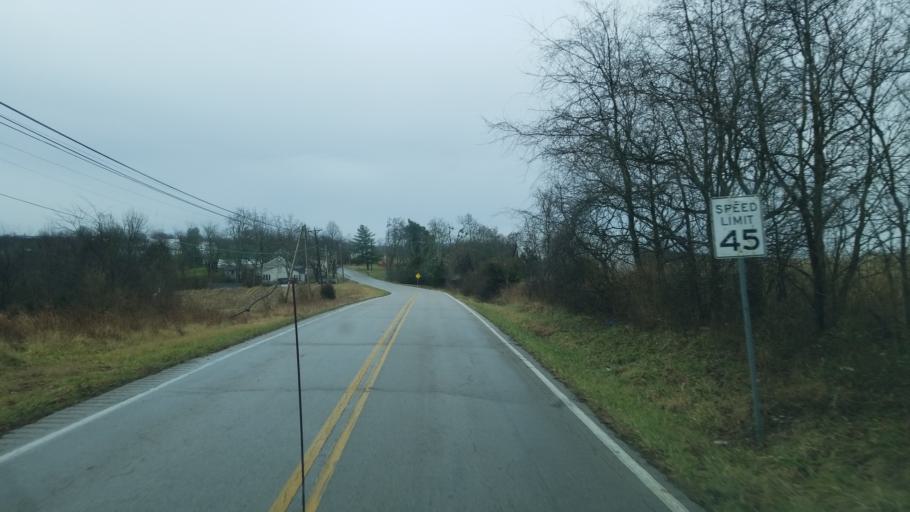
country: US
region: Kentucky
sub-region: Mason County
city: Maysville
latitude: 38.5939
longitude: -83.6703
